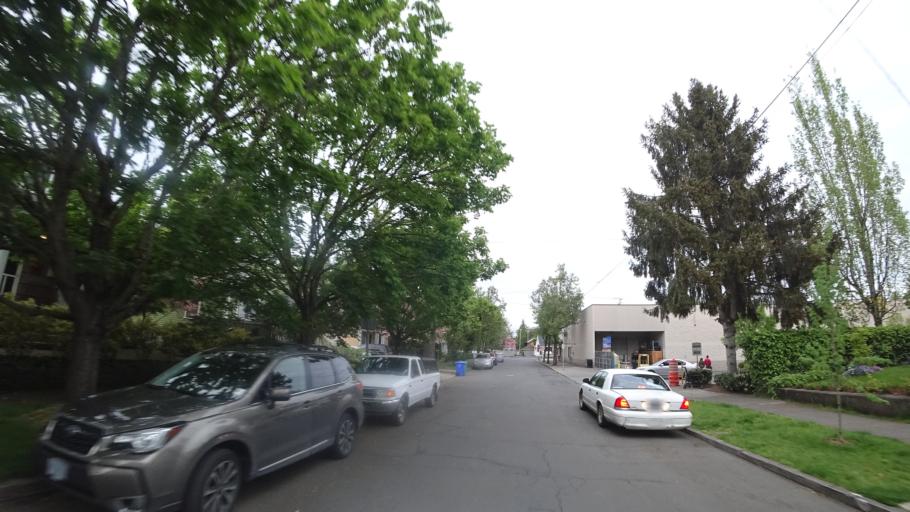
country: US
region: Oregon
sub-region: Clackamas County
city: Milwaukie
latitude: 45.4765
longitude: -122.6502
